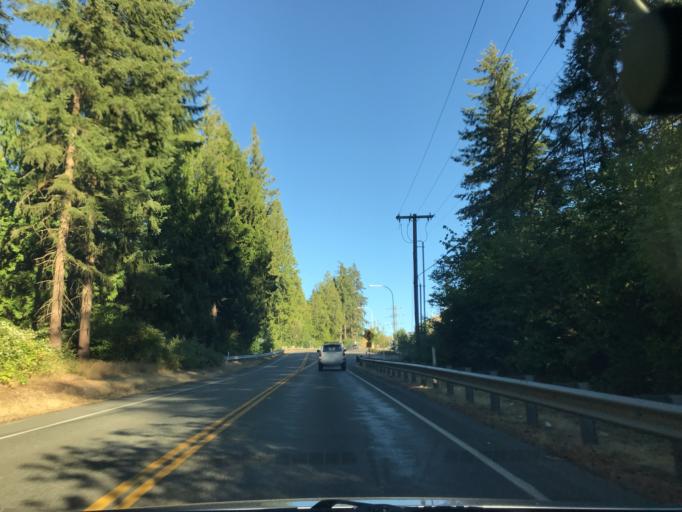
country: US
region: Washington
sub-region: King County
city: Pacific
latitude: 47.2655
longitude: -122.2015
